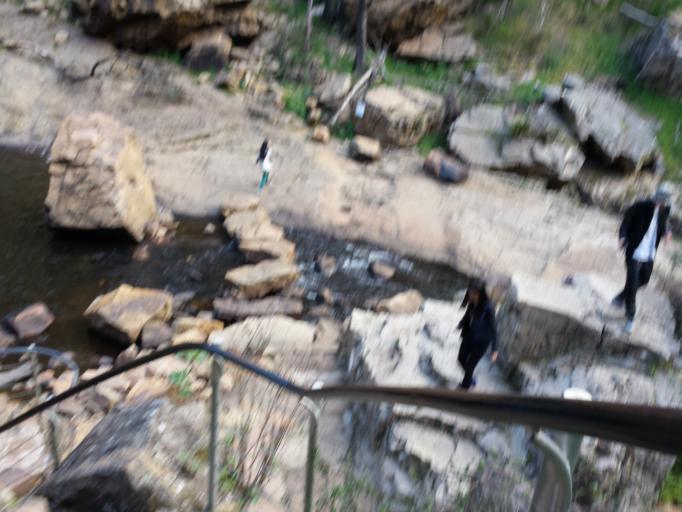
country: AU
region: Victoria
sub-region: Northern Grampians
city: Stawell
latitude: -37.1109
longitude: 142.4088
